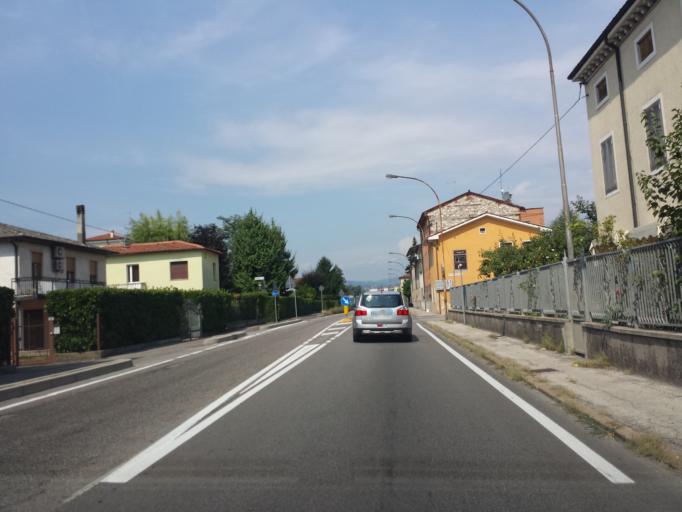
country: IT
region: Veneto
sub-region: Provincia di Vicenza
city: Montecchio Maggiore-Alte Ceccato
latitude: 45.5052
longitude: 11.4043
